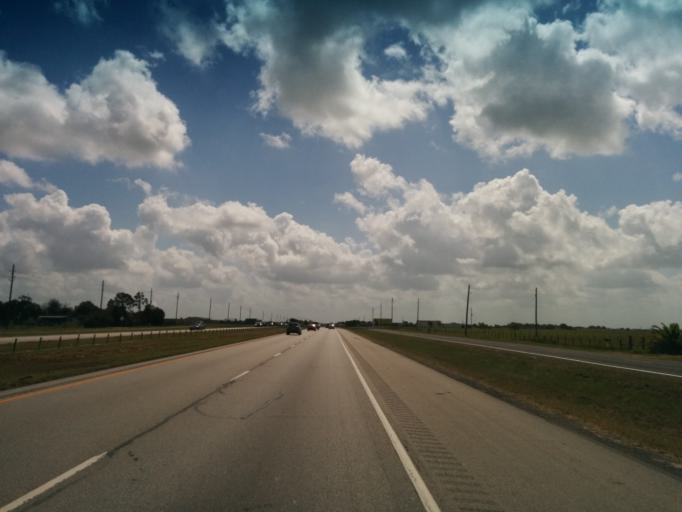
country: US
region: Texas
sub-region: Austin County
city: Sealy
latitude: 29.7547
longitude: -96.2498
